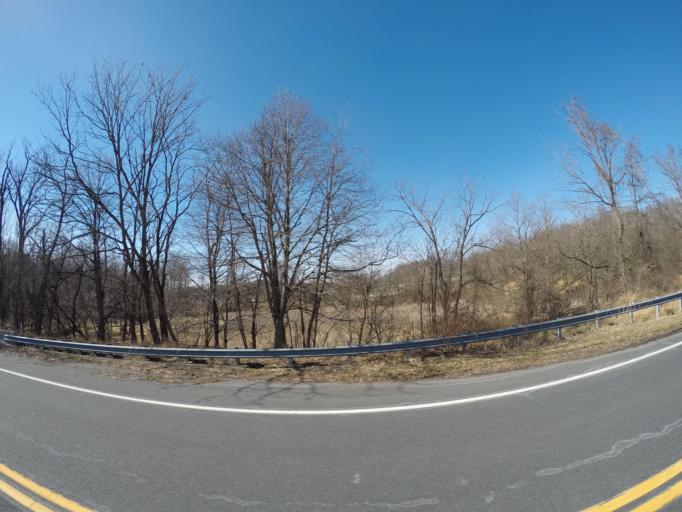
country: US
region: Maryland
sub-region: Howard County
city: Columbia
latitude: 39.2469
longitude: -76.8274
